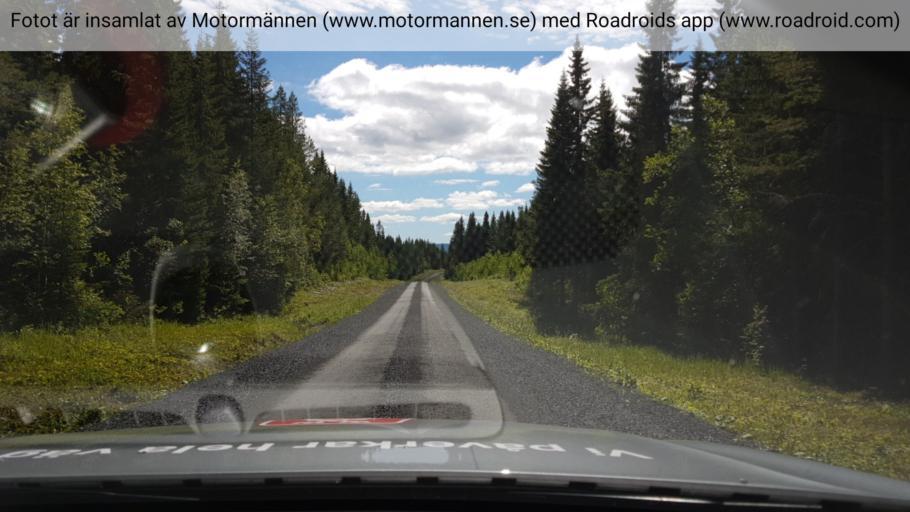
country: SE
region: Jaemtland
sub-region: Krokoms Kommun
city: Valla
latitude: 63.3352
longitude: 13.8384
